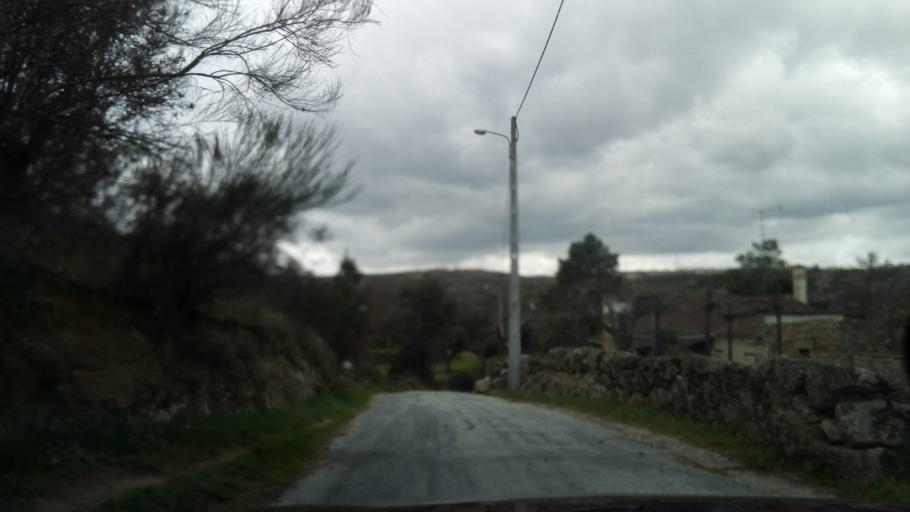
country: PT
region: Guarda
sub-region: Fornos de Algodres
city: Fornos de Algodres
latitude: 40.5846
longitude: -7.5636
